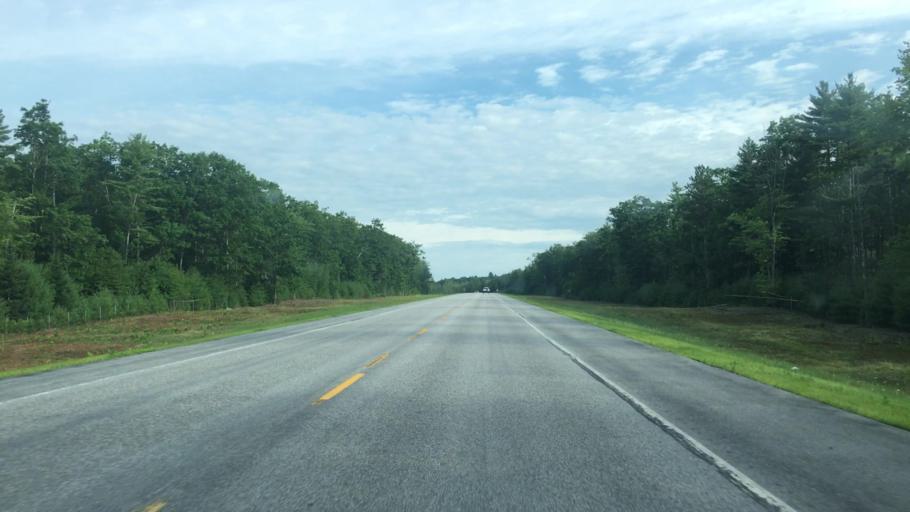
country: US
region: Maine
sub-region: Cumberland County
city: Gorham
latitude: 43.6617
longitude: -70.4511
